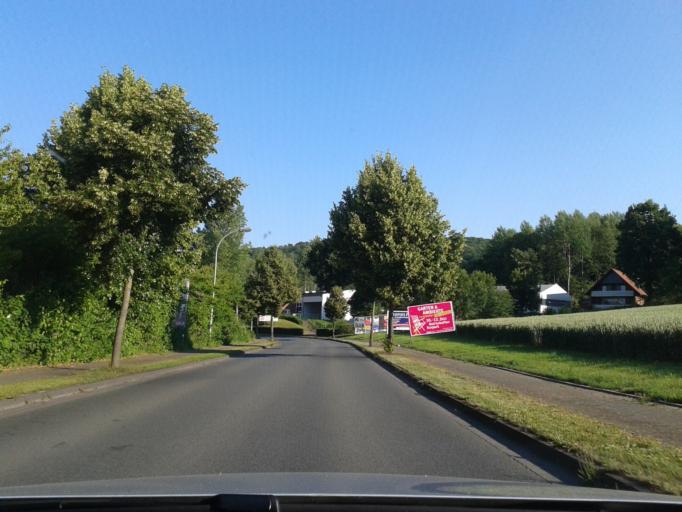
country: DE
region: North Rhine-Westphalia
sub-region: Regierungsbezirk Detmold
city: Dorentrup
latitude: 52.0341
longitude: 8.9986
